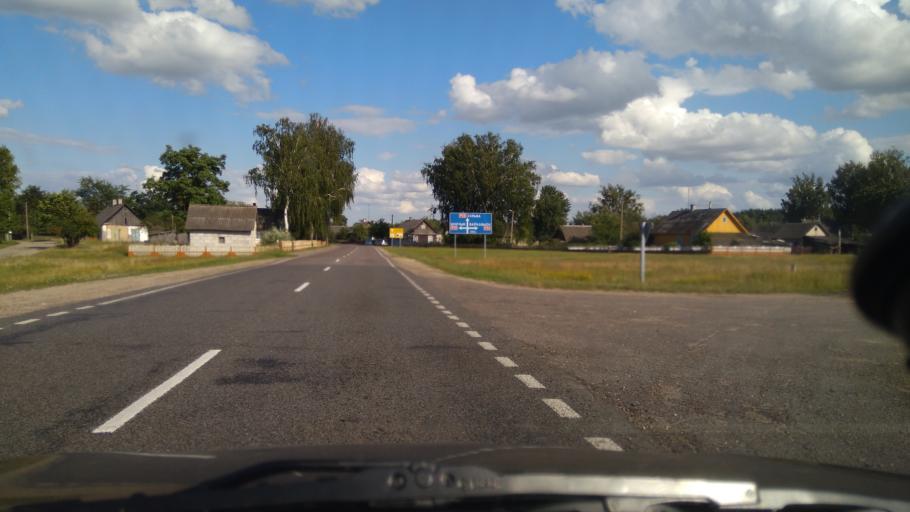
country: BY
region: Grodnenskaya
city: Masty
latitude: 53.3516
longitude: 24.6188
